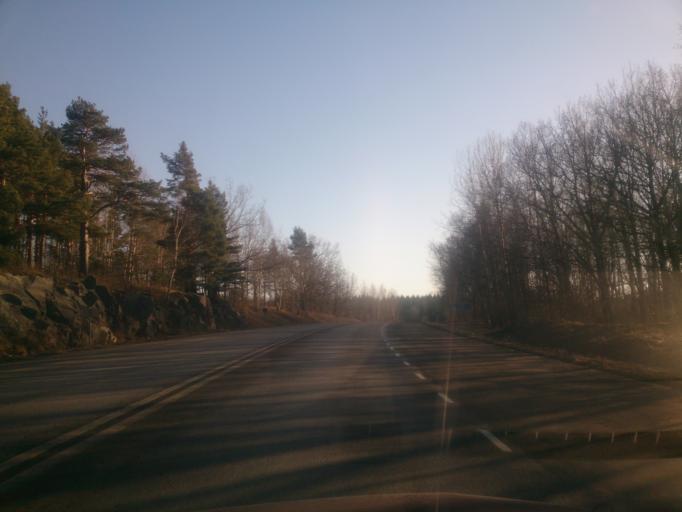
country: SE
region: OEstergoetland
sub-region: Norrkopings Kommun
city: Kimstad
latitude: 58.5078
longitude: 15.9820
